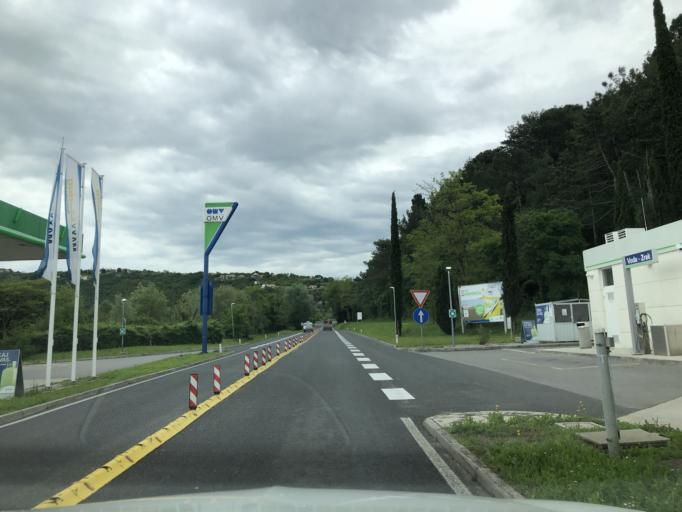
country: SI
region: Piran-Pirano
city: Seca
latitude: 45.5005
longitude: 13.6103
